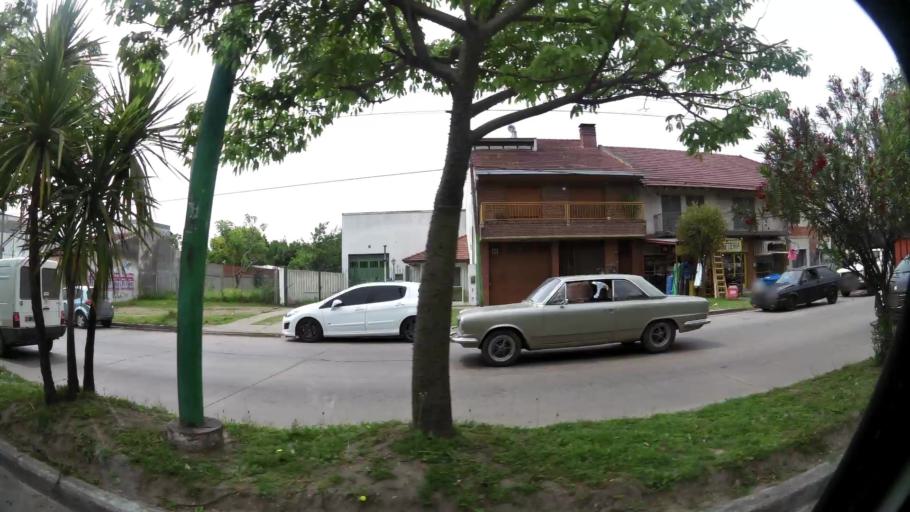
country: AR
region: Buenos Aires
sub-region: Partido de La Plata
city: La Plata
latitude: -34.9233
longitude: -58.0188
